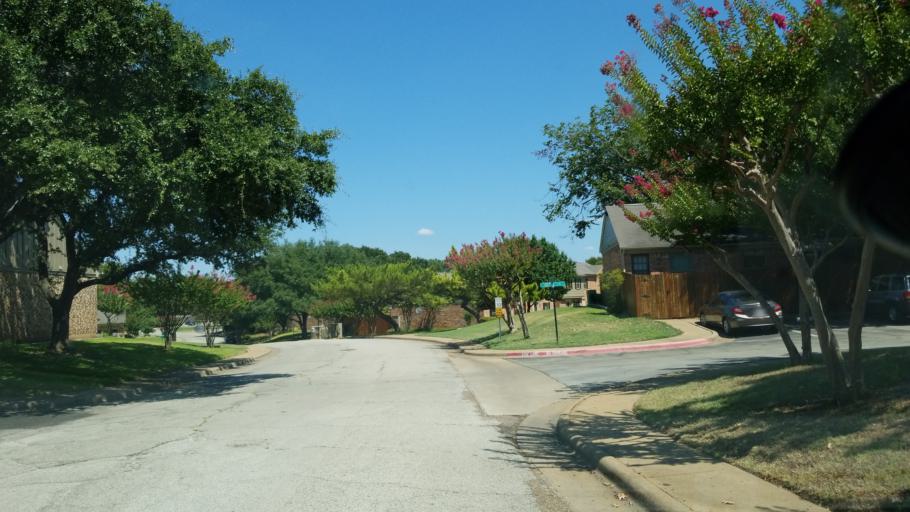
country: US
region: Texas
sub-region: Dallas County
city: Cockrell Hill
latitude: 32.7160
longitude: -96.8910
